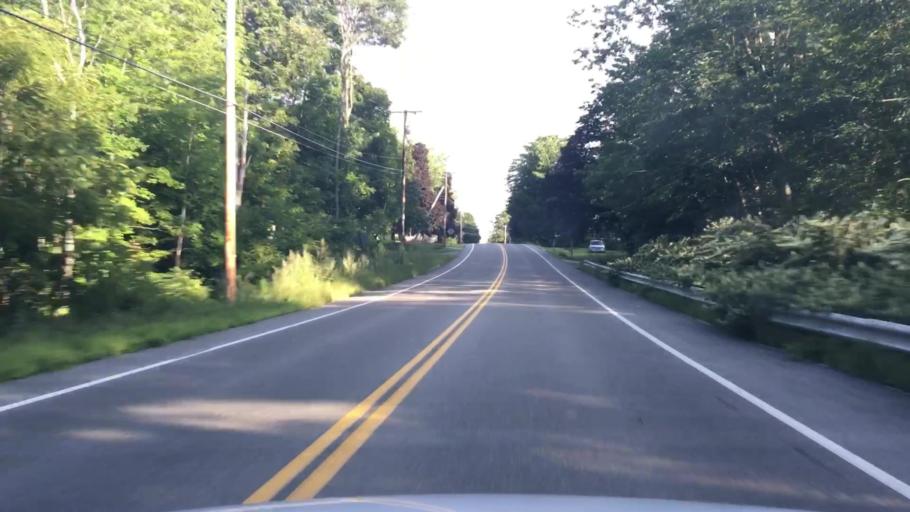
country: US
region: Maine
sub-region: Cumberland County
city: South Windham
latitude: 43.7510
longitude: -70.4311
